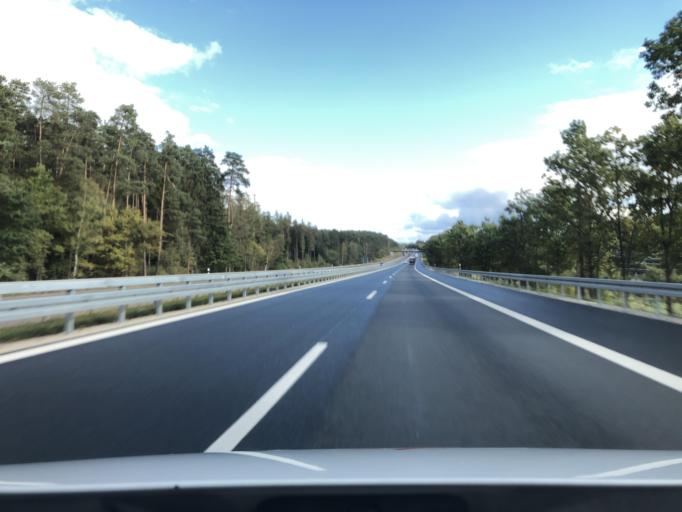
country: DE
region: Bavaria
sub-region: Upper Palatinate
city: Ebermannsdorf
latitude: 49.3990
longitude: 11.9440
